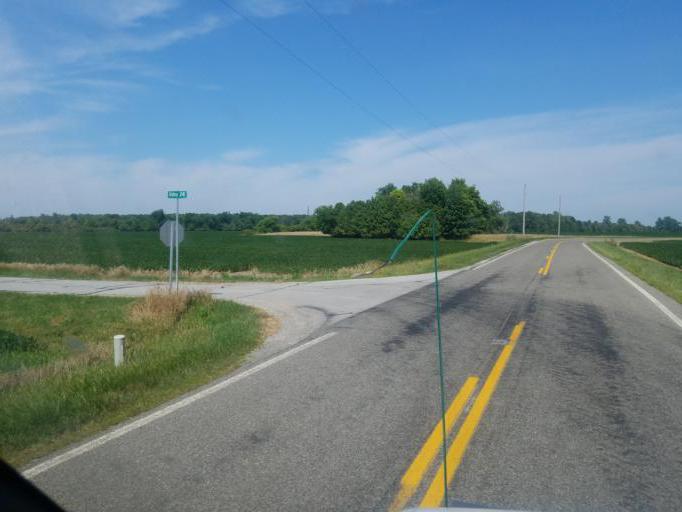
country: US
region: Ohio
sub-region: Shelby County
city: Jackson Center
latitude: 40.4976
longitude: -84.0122
